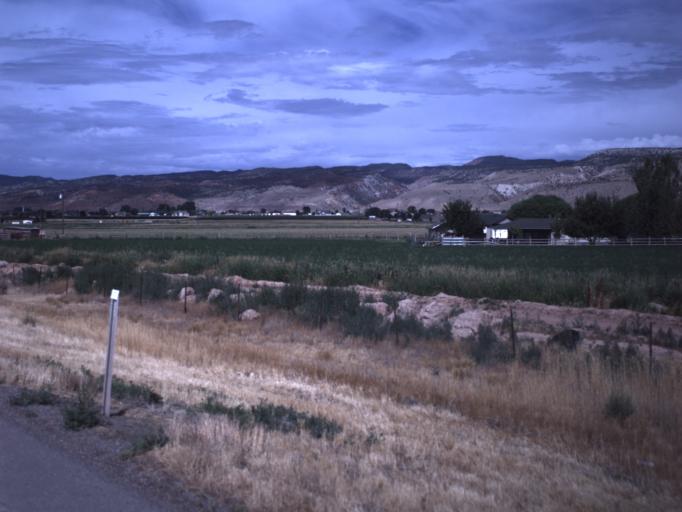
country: US
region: Utah
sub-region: Sevier County
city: Richfield
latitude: 38.7854
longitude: -112.0543
